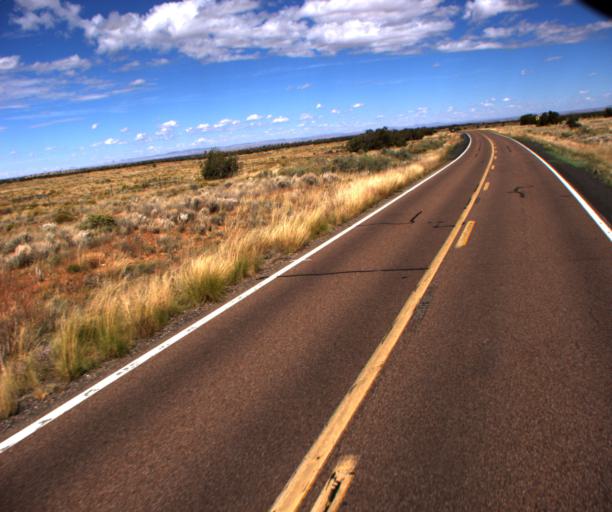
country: US
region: Arizona
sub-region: Navajo County
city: Holbrook
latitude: 34.6808
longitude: -110.3111
